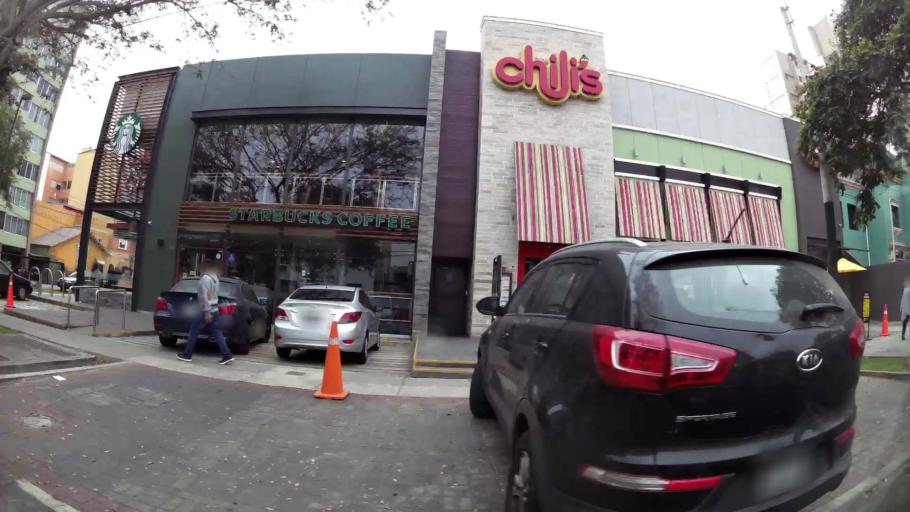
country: PE
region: Lima
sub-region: Lima
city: San Isidro
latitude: -12.0915
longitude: -77.0403
